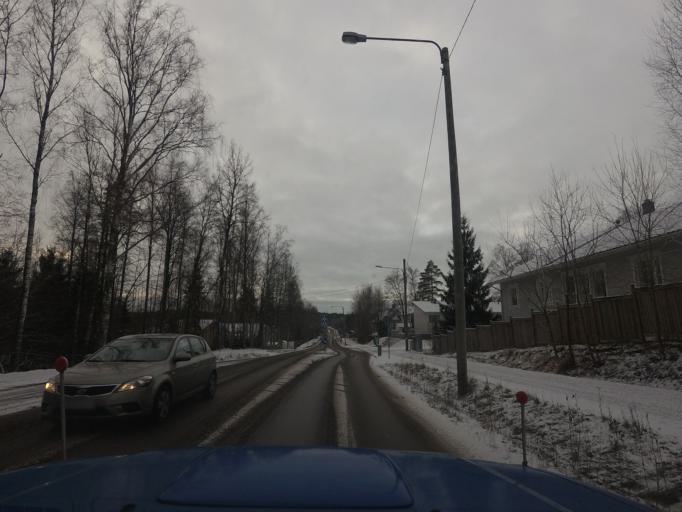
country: FI
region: Uusimaa
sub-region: Helsinki
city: Kilo
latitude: 60.2433
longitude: 24.7741
